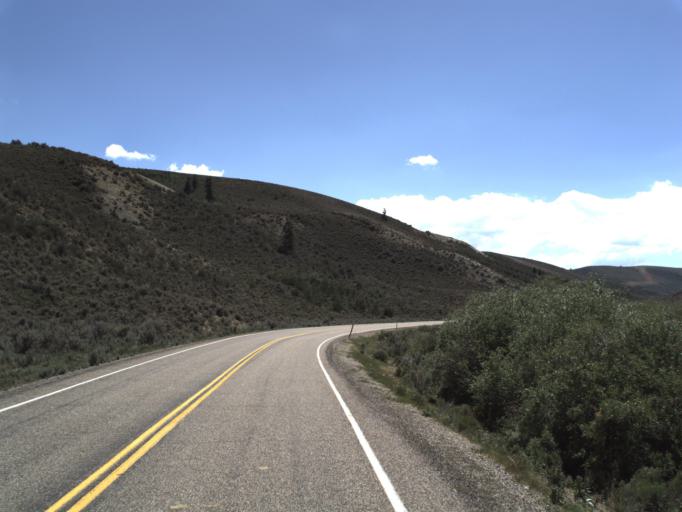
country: US
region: Utah
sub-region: Rich County
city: Randolph
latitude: 41.4997
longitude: -111.3210
